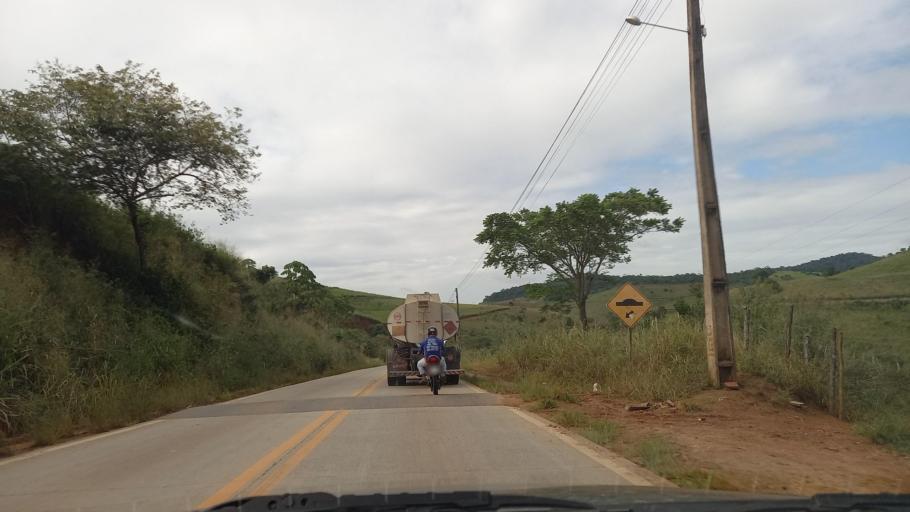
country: BR
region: Pernambuco
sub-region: Maraial
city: Maraial
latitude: -8.7490
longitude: -35.8071
